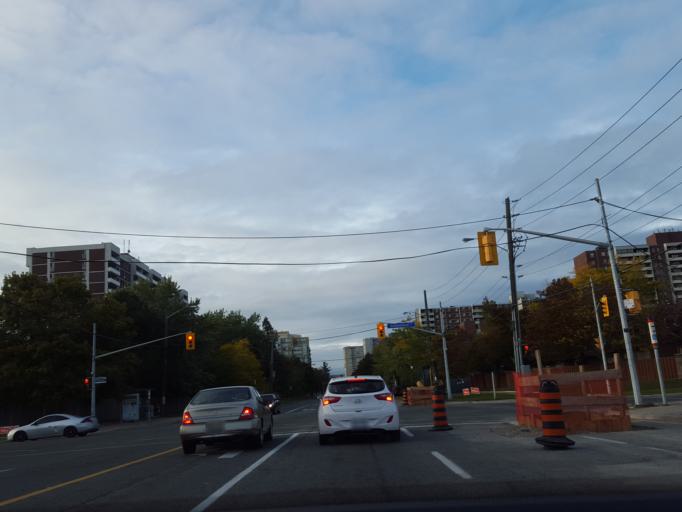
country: CA
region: Ontario
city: Scarborough
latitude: 43.7919
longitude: -79.3137
